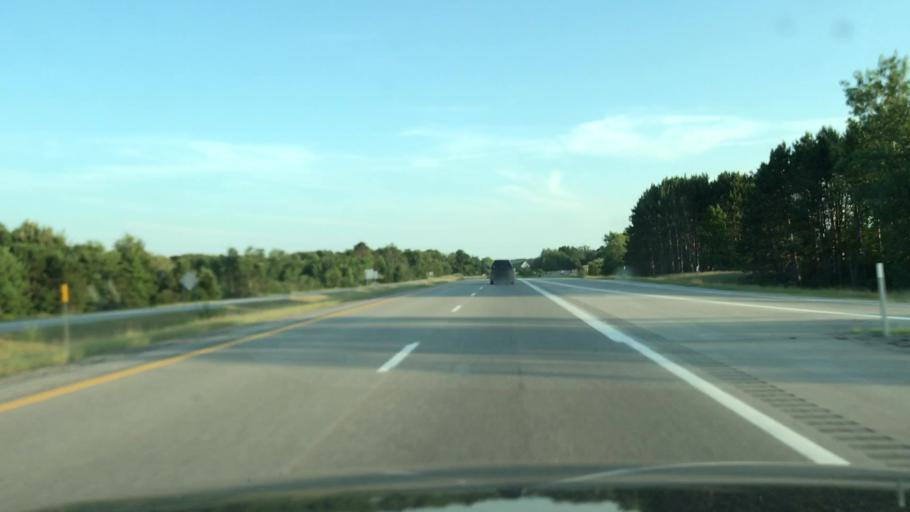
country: US
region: Michigan
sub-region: Osceola County
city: Reed City
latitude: 43.8829
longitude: -85.5282
